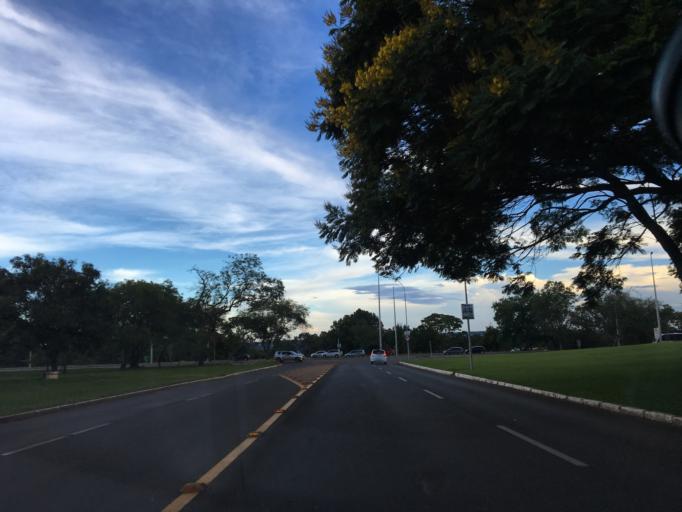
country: BR
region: Federal District
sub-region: Brasilia
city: Brasilia
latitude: -15.8070
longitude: -47.8587
